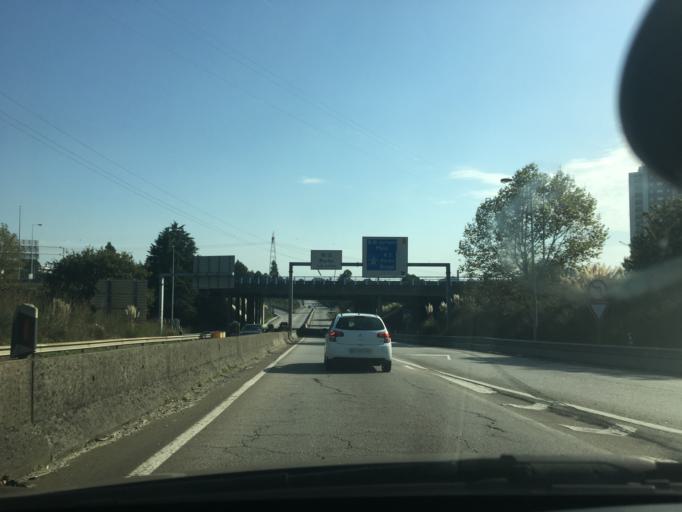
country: PT
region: Porto
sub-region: Maia
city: Gemunde
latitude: 41.2417
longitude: -8.6469
